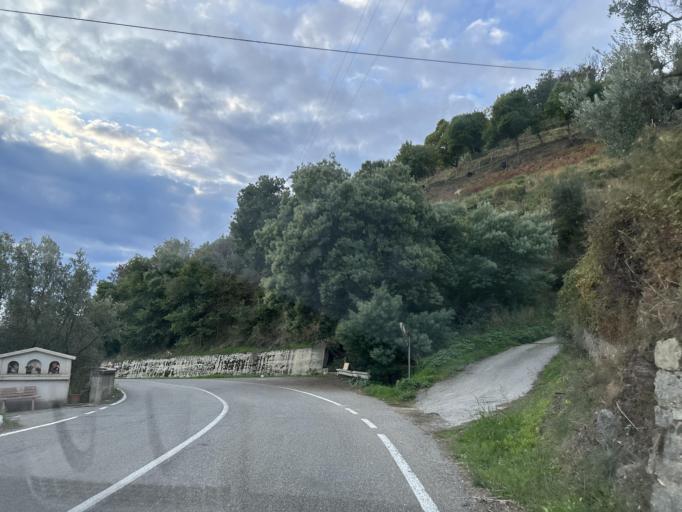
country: IT
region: Calabria
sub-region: Provincia di Catanzaro
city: Montauro
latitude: 38.7518
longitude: 16.5071
